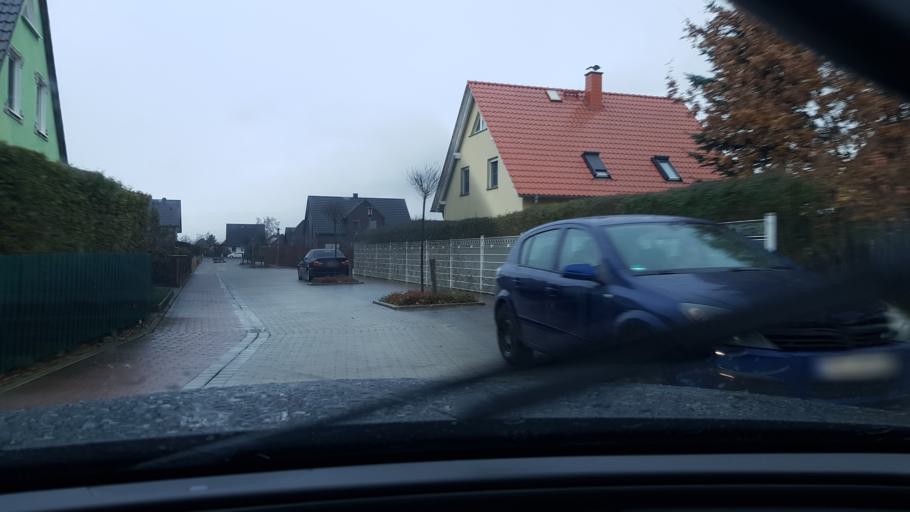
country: DE
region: Saxony-Anhalt
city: Oebisfelde
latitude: 52.4325
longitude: 11.0005
